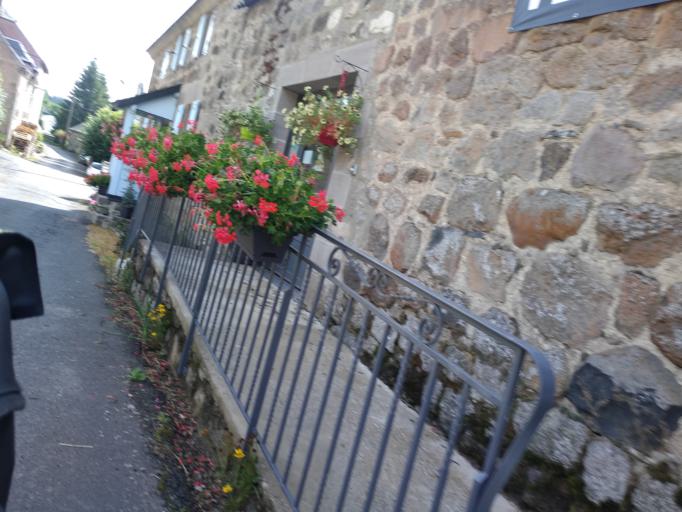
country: FR
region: Auvergne
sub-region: Departement du Cantal
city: Murat
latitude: 45.1380
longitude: 2.7476
